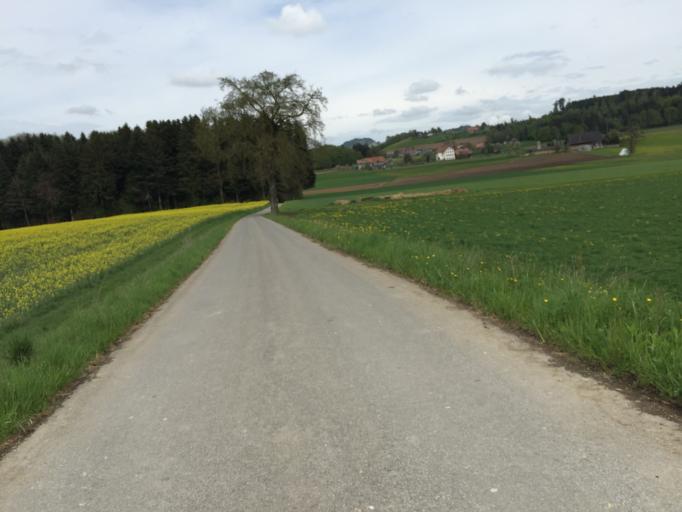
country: CH
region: Bern
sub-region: Bern-Mittelland District
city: Rubigen
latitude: 46.9187
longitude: 7.5328
